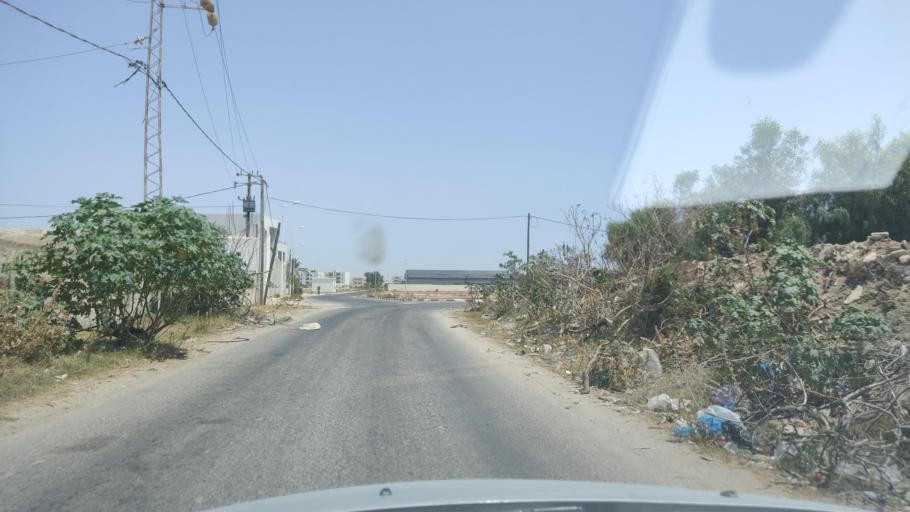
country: TN
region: Safaqis
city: Sfax
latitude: 34.7070
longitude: 10.7196
